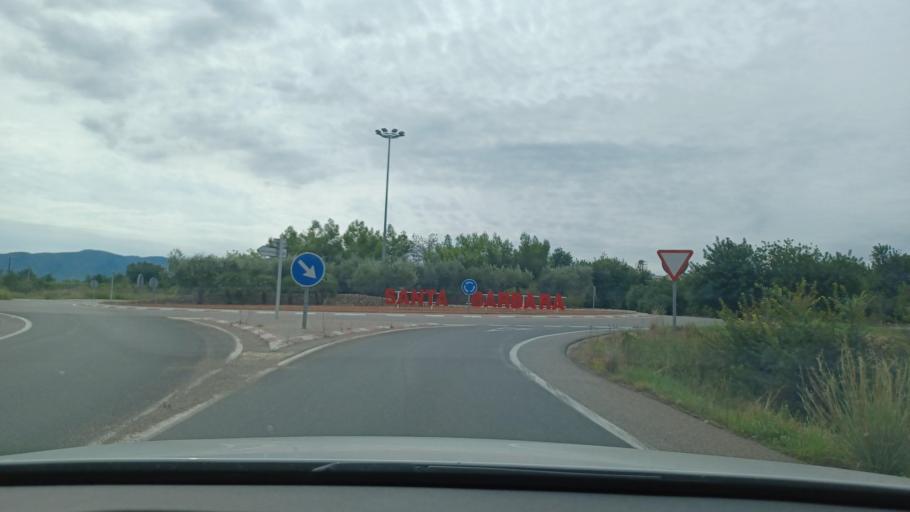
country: ES
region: Catalonia
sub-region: Provincia de Tarragona
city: Santa Barbara
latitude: 40.7240
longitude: 0.5030
